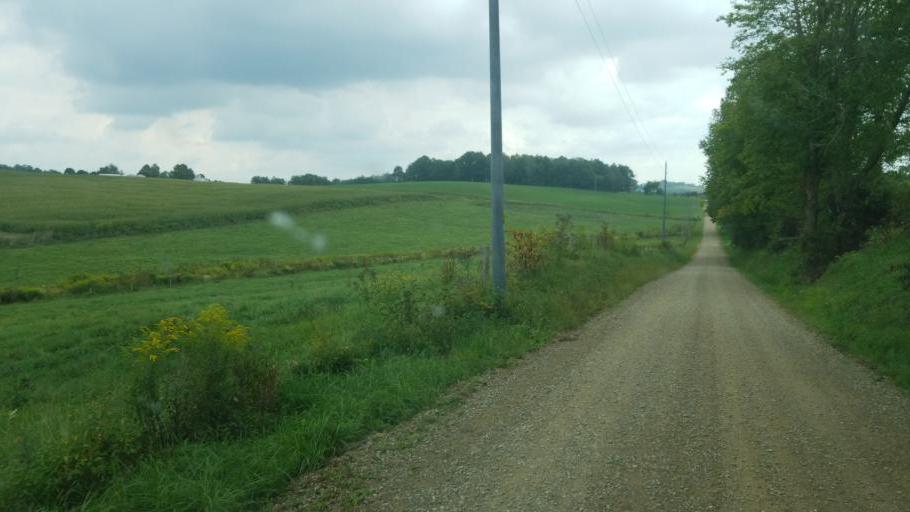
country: US
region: Ohio
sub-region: Knox County
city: Danville
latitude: 40.4477
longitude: -82.3148
